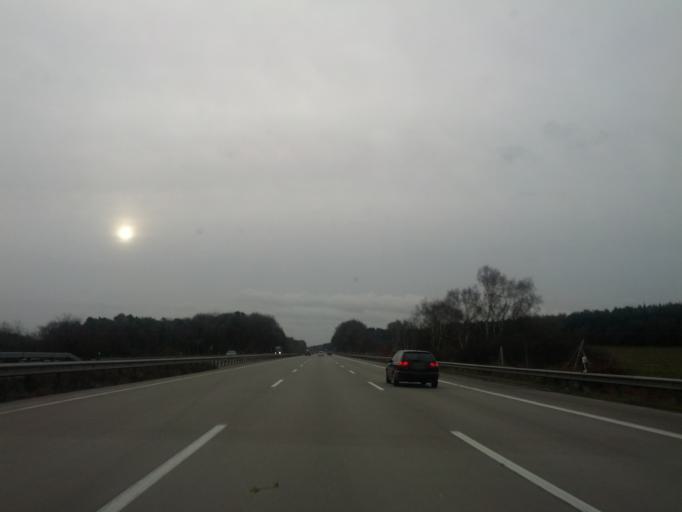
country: DE
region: Lower Saxony
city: Brackel
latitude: 53.2908
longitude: 10.0773
